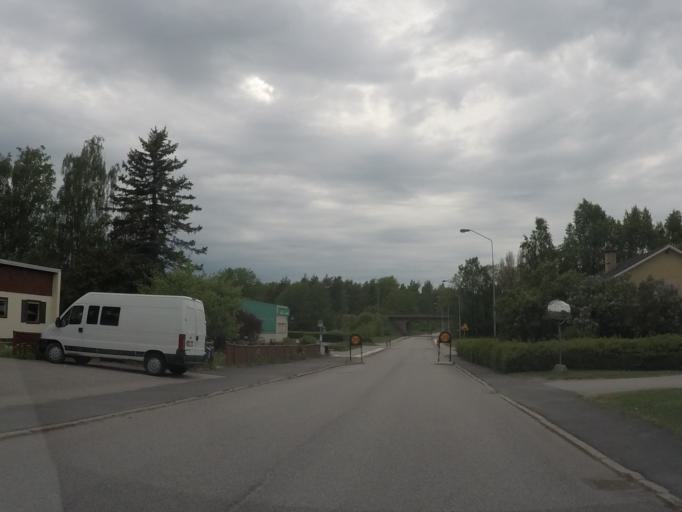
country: SE
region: Soedermanland
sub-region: Flens Kommun
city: Malmkoping
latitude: 59.0709
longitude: 16.8278
